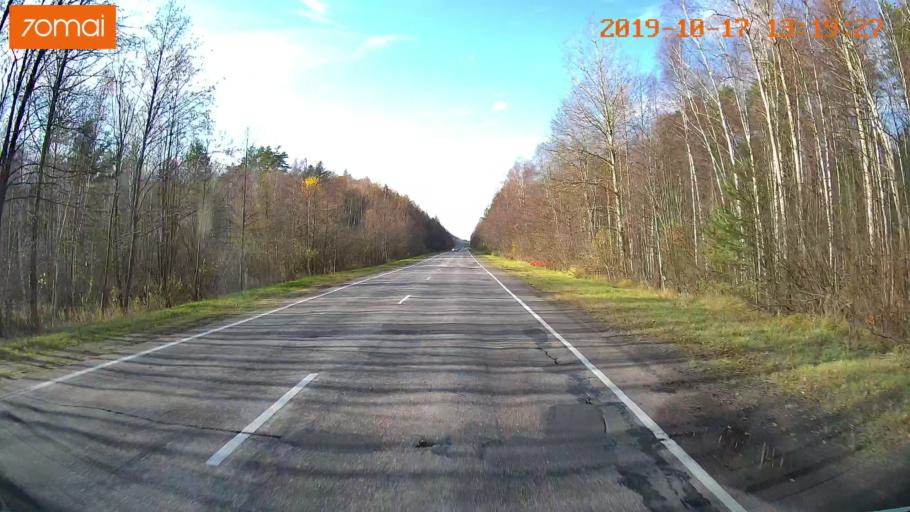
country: RU
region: Rjazan
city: Gus'-Zheleznyy
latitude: 55.0695
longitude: 41.0739
